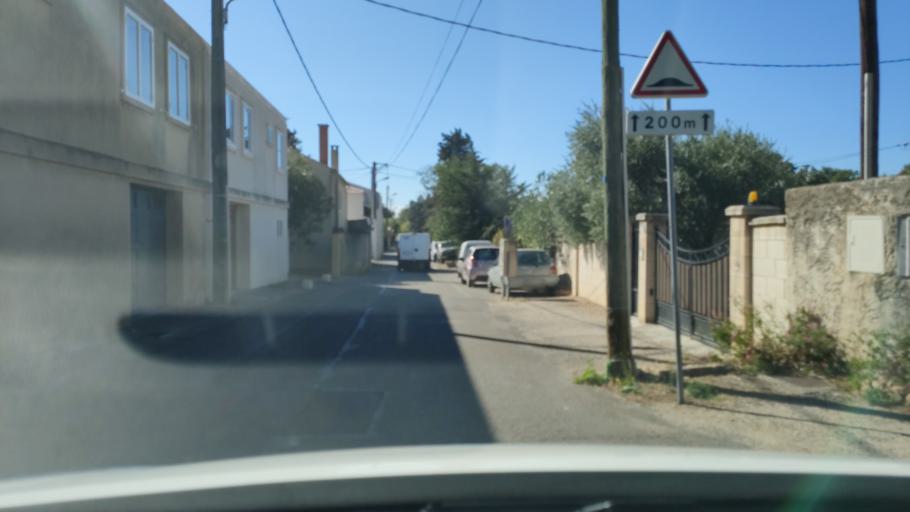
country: FR
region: Provence-Alpes-Cote d'Azur
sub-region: Departement du Vaucluse
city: Morieres-les-Avignon
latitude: 43.9436
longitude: 4.9036
